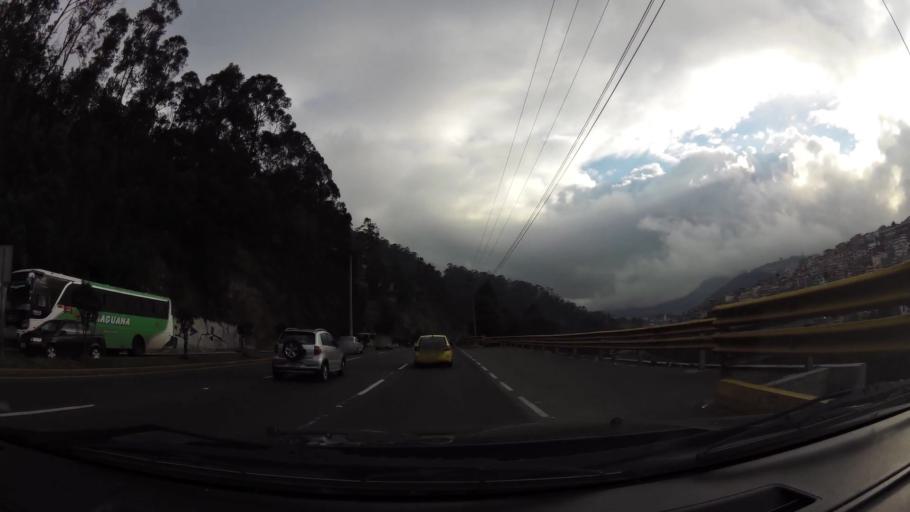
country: EC
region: Pichincha
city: Quito
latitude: -0.2303
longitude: -78.4982
